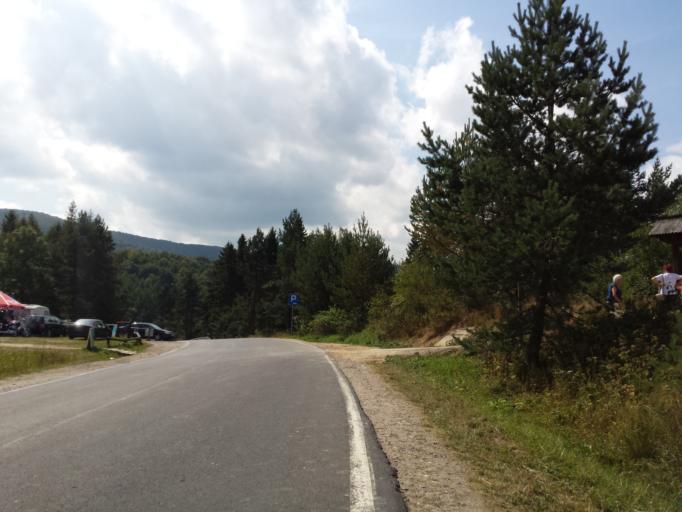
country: PL
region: Subcarpathian Voivodeship
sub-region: Powiat bieszczadzki
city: Lutowiska
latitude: 49.1417
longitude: 22.5483
